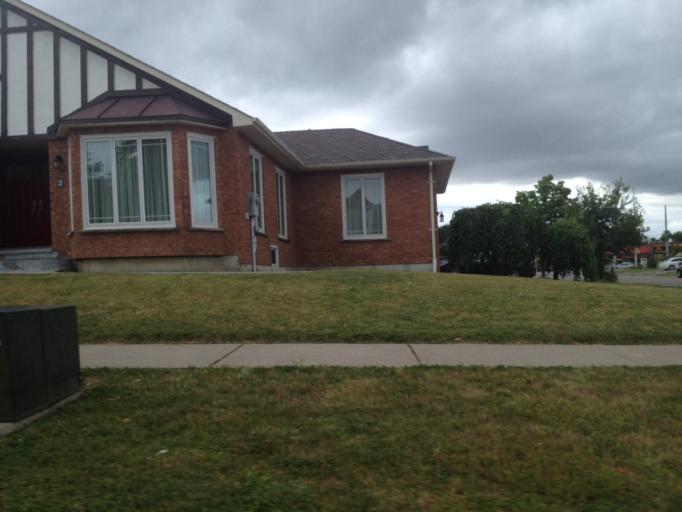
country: CA
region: Ontario
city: Brampton
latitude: 43.6725
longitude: -79.7241
